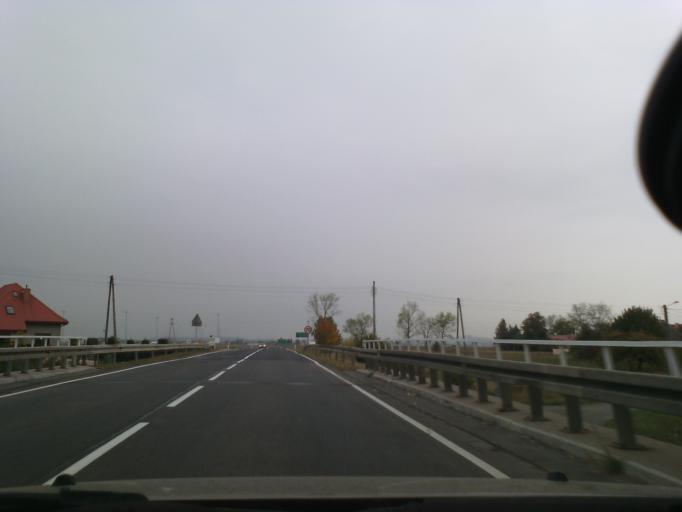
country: PL
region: Lower Silesian Voivodeship
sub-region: Powiat walbrzyski
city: Stare Bogaczowice
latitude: 50.9127
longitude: 16.2510
